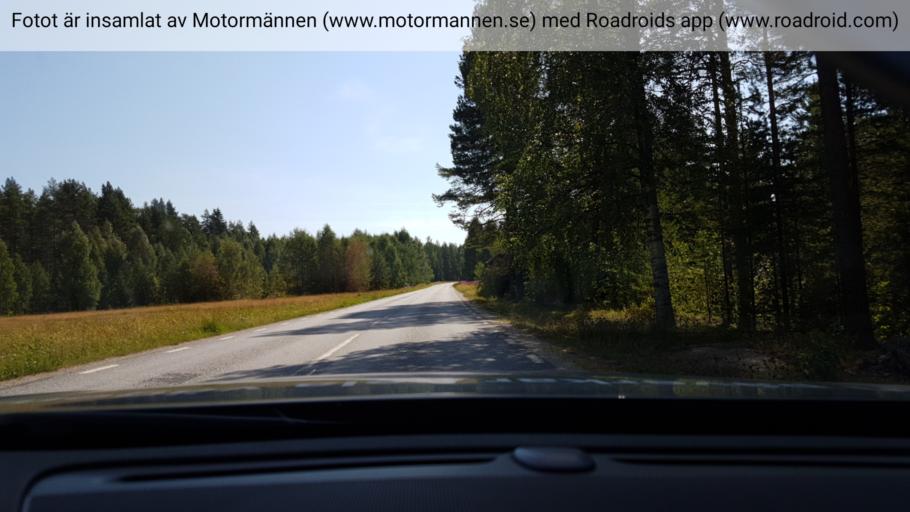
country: SE
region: Vaesterbotten
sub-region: Vindelns Kommun
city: Vindeln
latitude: 64.2777
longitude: 19.6284
